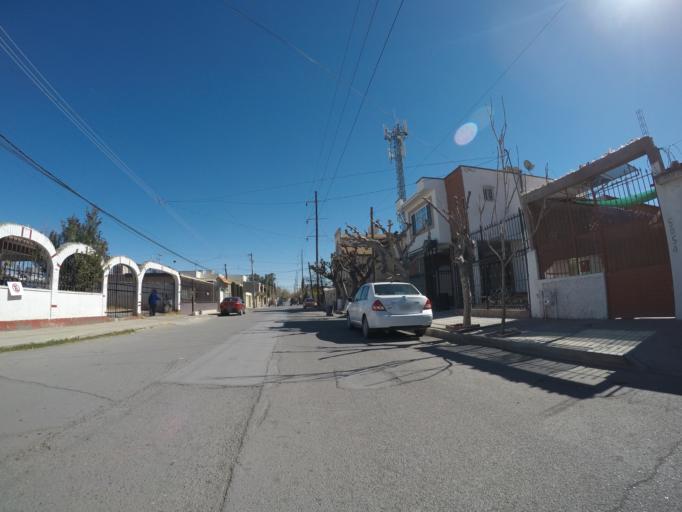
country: MX
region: Chihuahua
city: Ciudad Juarez
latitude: 31.7321
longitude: -106.4401
